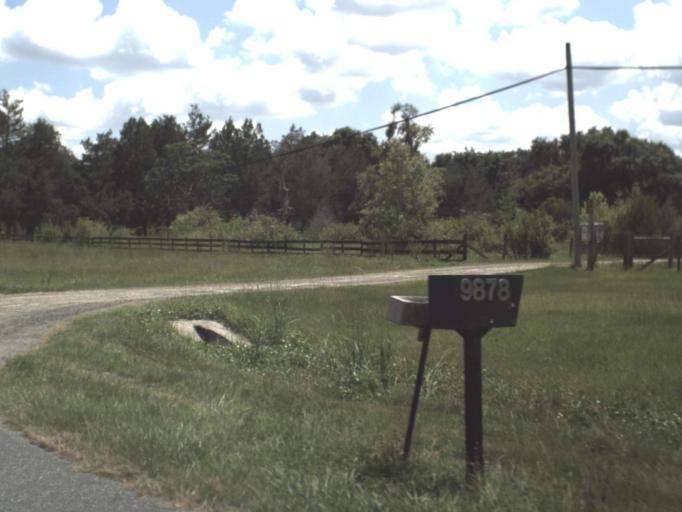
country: US
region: Florida
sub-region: Columbia County
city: Watertown
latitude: 30.0572
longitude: -82.5993
